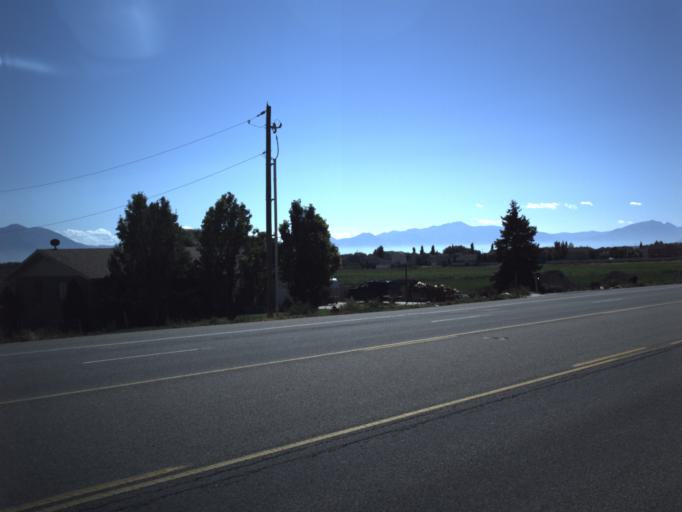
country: US
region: Utah
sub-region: Utah County
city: Saratoga Springs
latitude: 40.3813
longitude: -111.9165
